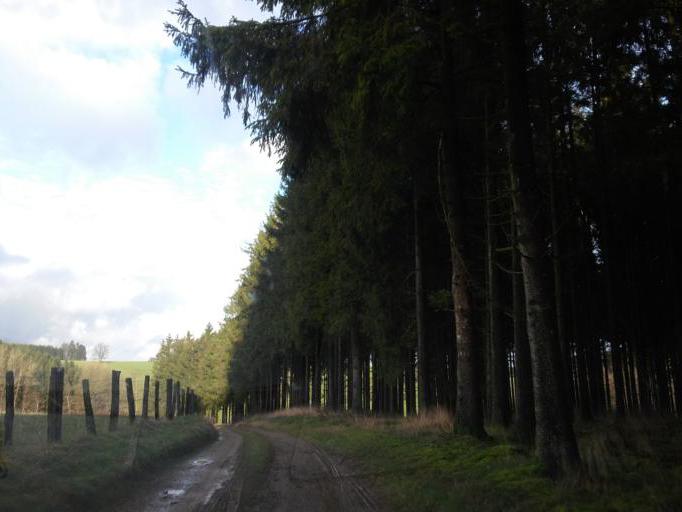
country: BE
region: Wallonia
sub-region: Province du Luxembourg
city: Neufchateau
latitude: 49.8023
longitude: 5.4311
